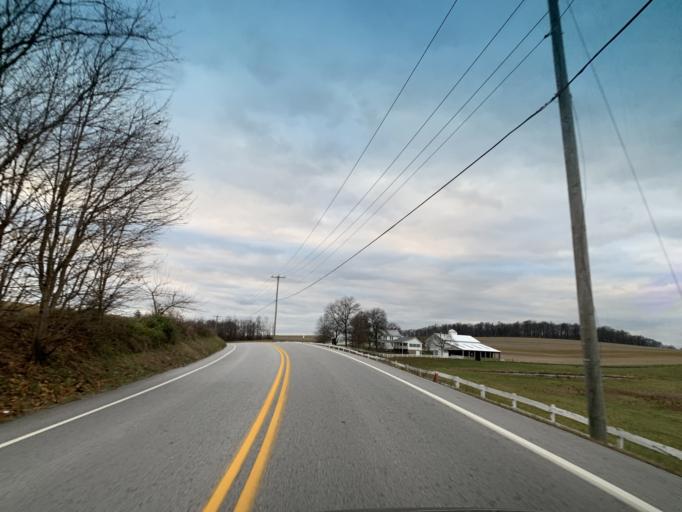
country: US
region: Pennsylvania
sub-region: York County
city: Stewartstown
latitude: 39.7827
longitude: -76.6206
